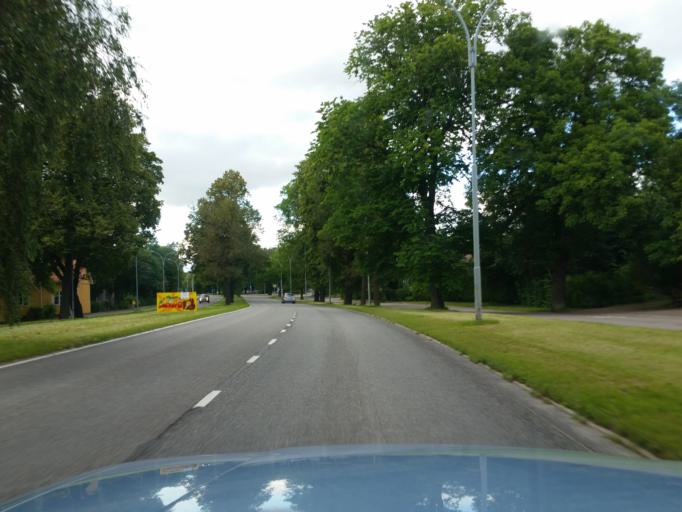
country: FI
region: Varsinais-Suomi
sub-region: Turku
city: Turku
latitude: 60.4387
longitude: 22.2915
